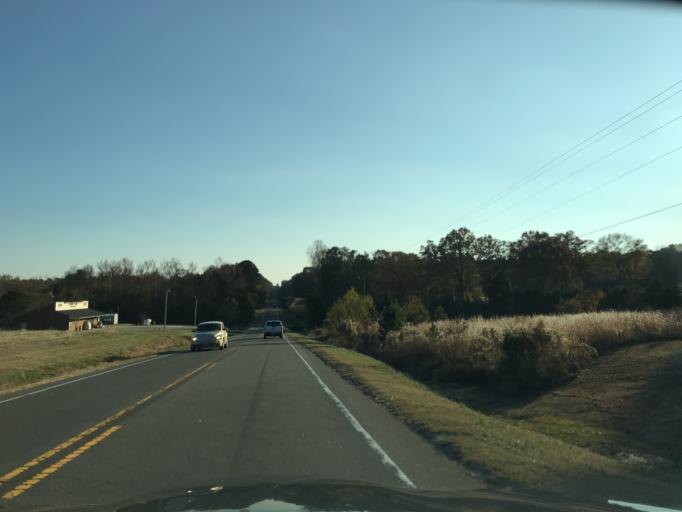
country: US
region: North Carolina
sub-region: Granville County
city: Creedmoor
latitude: 36.0513
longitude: -78.6979
